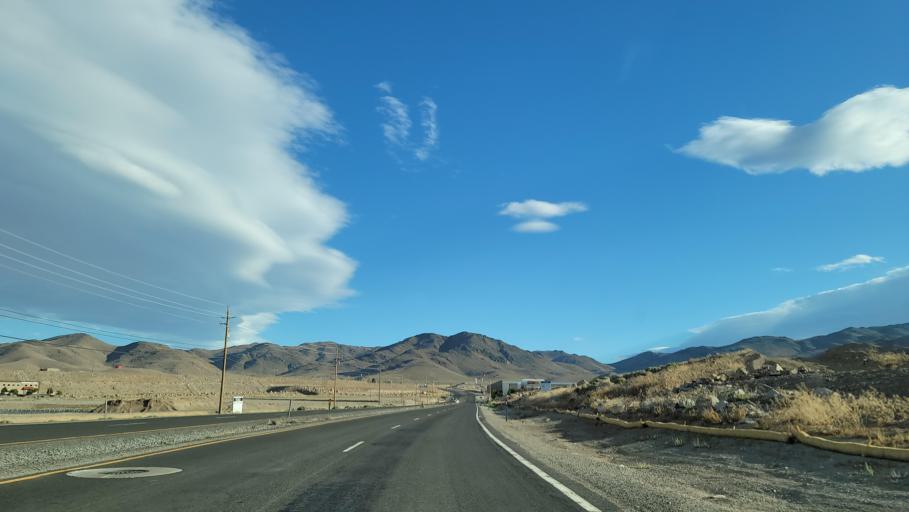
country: US
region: Nevada
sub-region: Lyon County
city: Stagecoach
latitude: 39.5448
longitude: -119.4847
